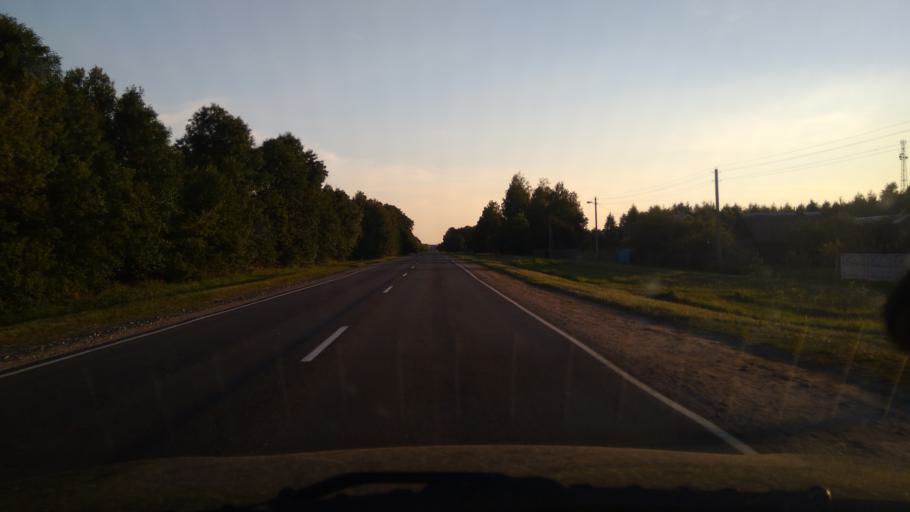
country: BY
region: Brest
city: Nyakhachava
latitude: 52.6455
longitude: 25.2084
